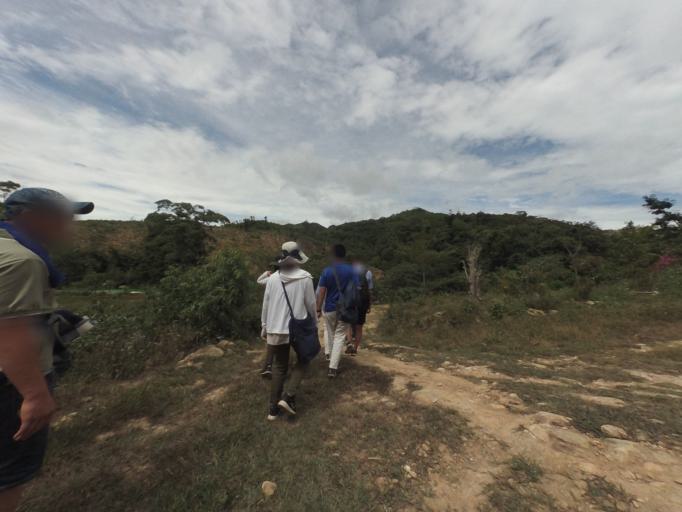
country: VN
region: Thua Thien-Hue
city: A Luoi
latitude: 16.3062
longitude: 107.2139
